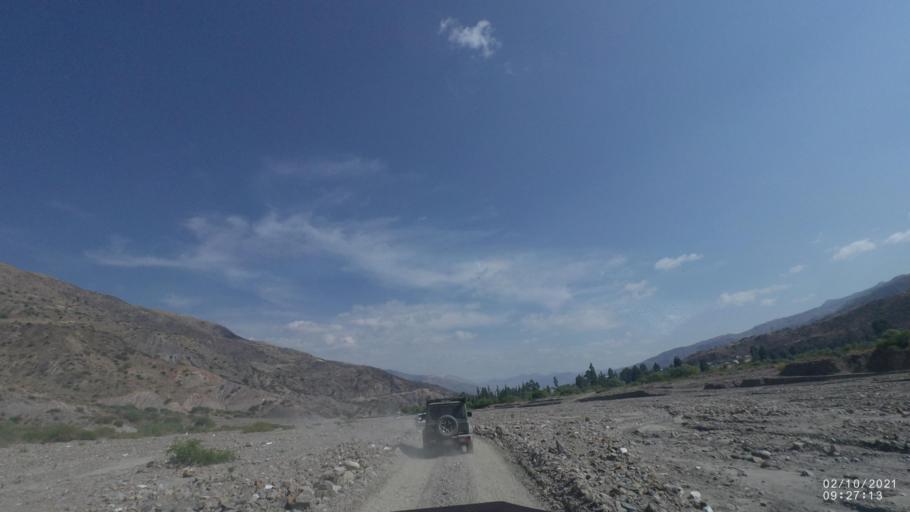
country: BO
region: Cochabamba
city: Irpa Irpa
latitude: -17.8564
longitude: -66.3147
